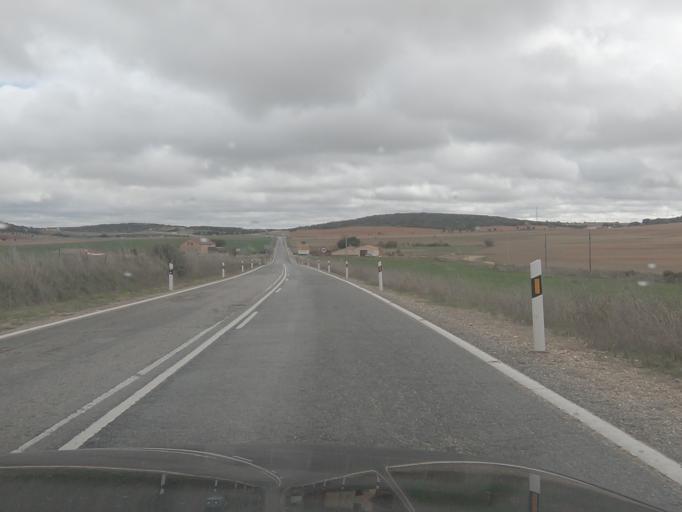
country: ES
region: Castille and Leon
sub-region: Provincia de Zamora
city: Montamarta
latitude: 41.6971
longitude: -5.8149
